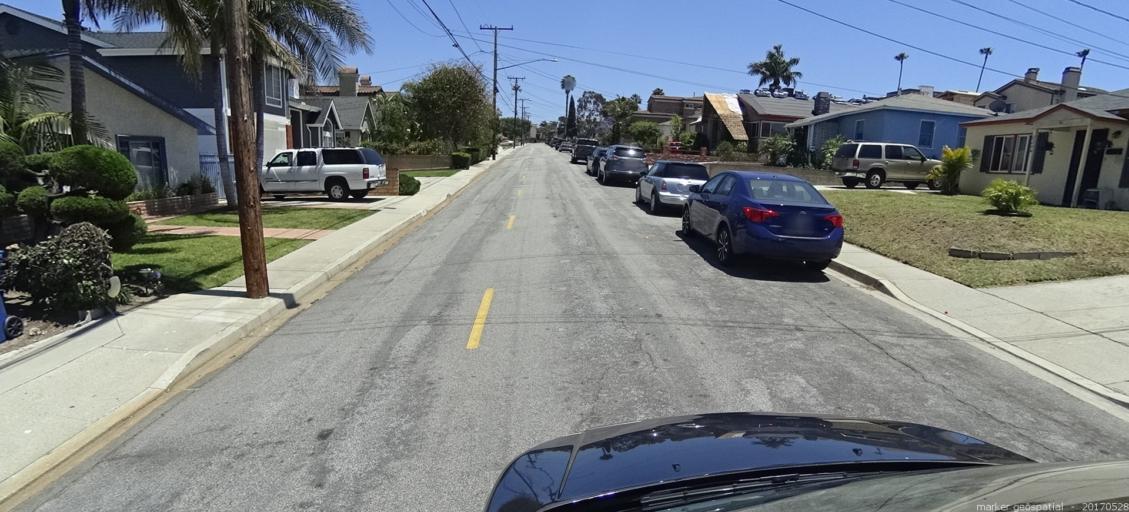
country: US
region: California
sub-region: Los Angeles County
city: Redondo Beach
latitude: 33.8634
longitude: -118.3724
